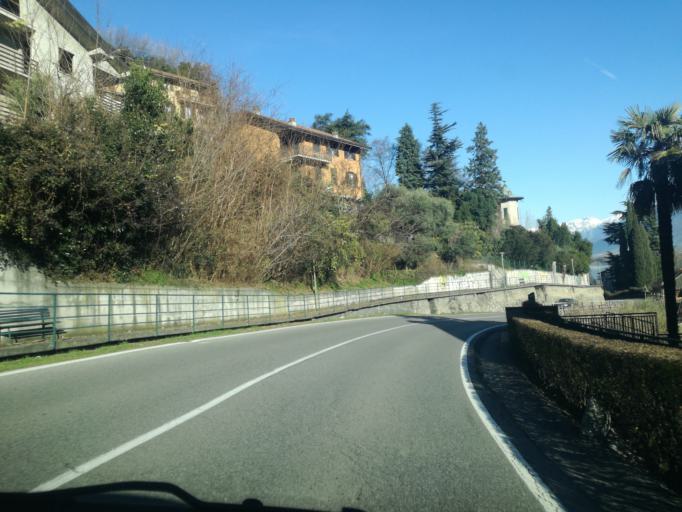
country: IT
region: Lombardy
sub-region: Provincia di Bergamo
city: Lovere
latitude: 45.8098
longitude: 10.0680
